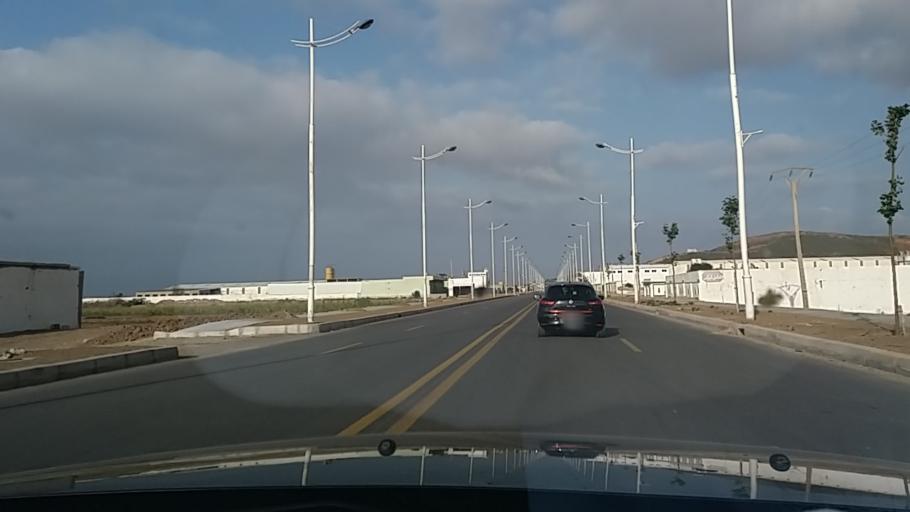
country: MA
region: Tanger-Tetouan
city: Tetouan
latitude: 35.5743
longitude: -5.3163
